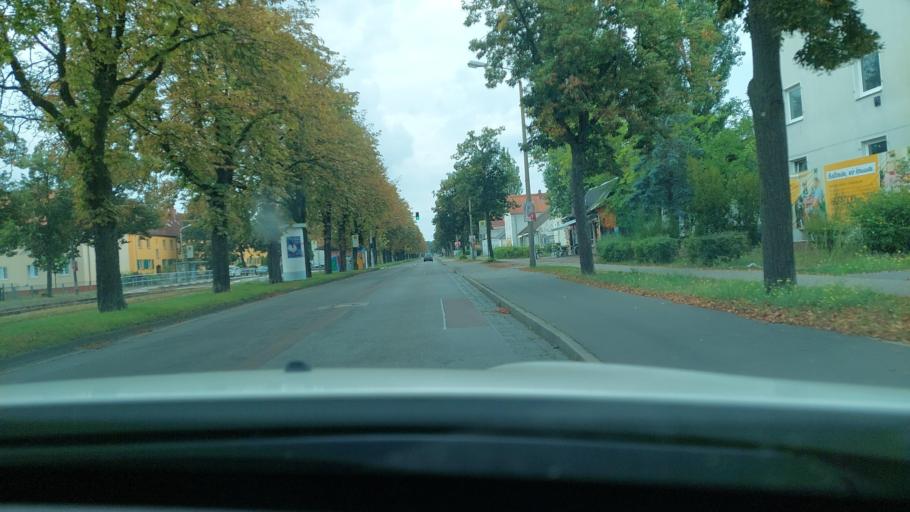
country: DE
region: Brandenburg
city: Brandenburg an der Havel
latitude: 52.4257
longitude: 12.5148
